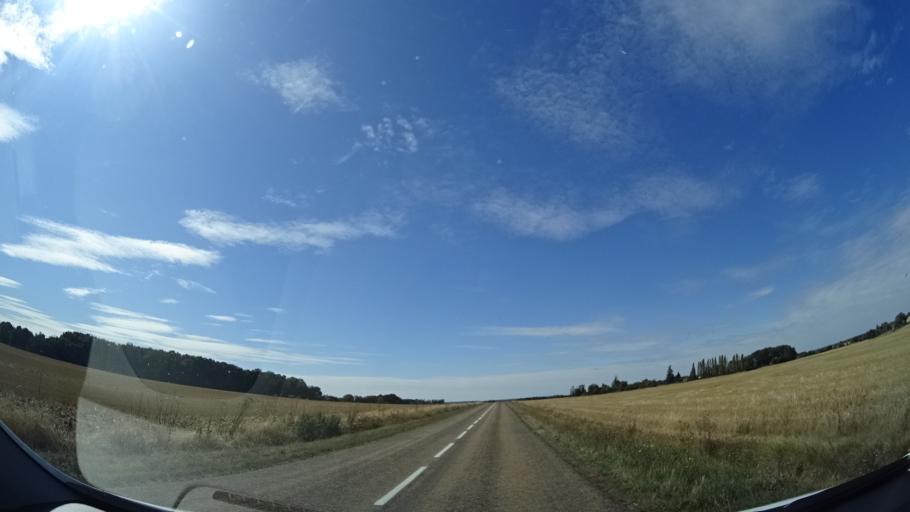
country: FR
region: Bourgogne
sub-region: Departement de l'Yonne
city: Cezy
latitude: 47.9289
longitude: 3.2776
